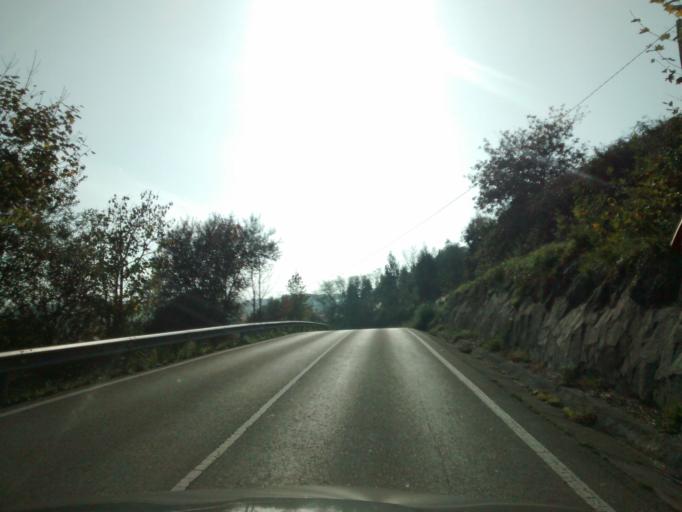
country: ES
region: Cantabria
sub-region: Provincia de Cantabria
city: Miengo
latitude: 43.4335
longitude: -3.9636
